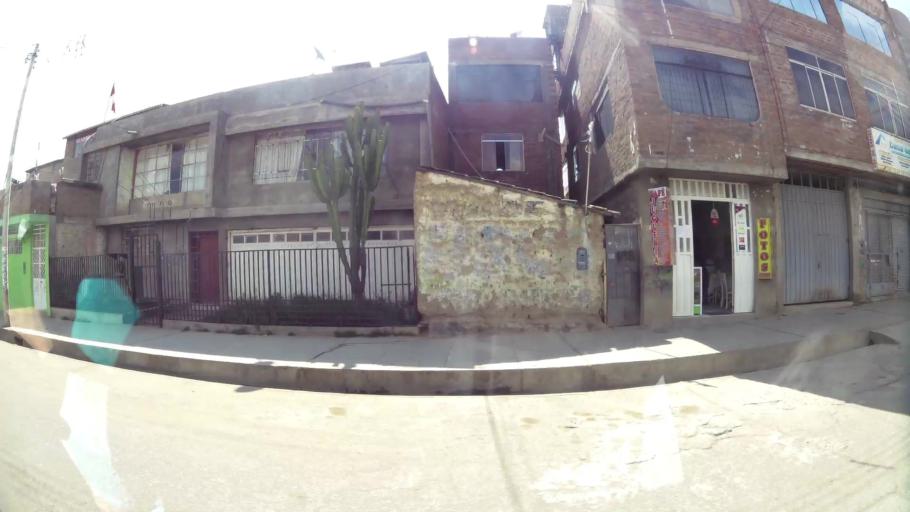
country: PE
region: Junin
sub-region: Provincia de Huancayo
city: Huancayo
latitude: -12.0753
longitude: -75.1956
